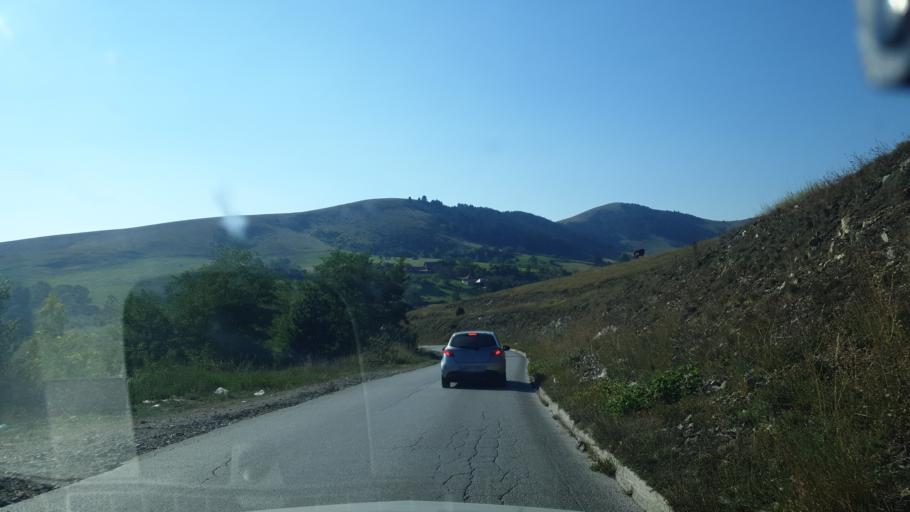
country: RS
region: Central Serbia
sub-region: Zlatiborski Okrug
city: Cajetina
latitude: 43.7194
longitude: 19.7609
